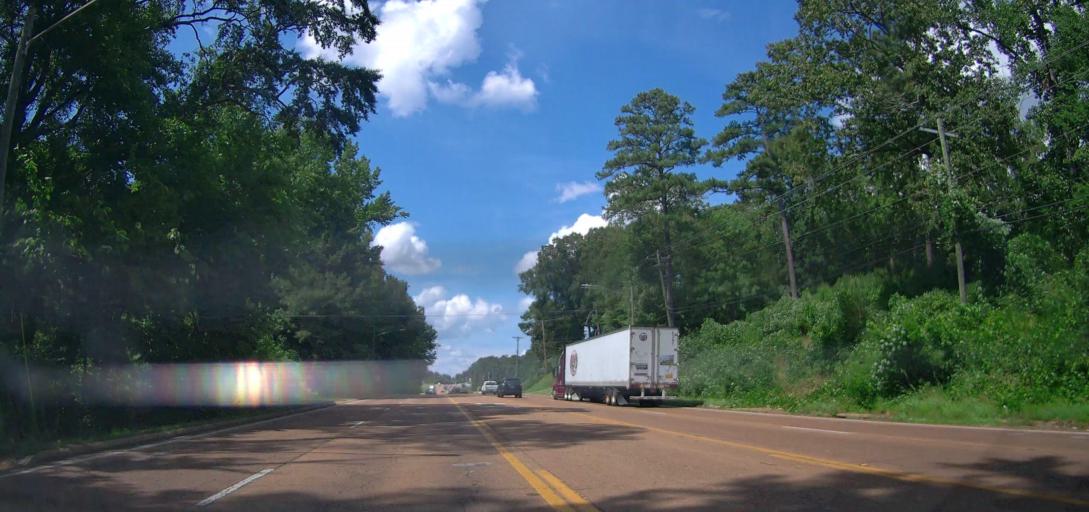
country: US
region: Mississippi
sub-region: Lowndes County
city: Columbus
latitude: 33.5547
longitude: -88.4331
